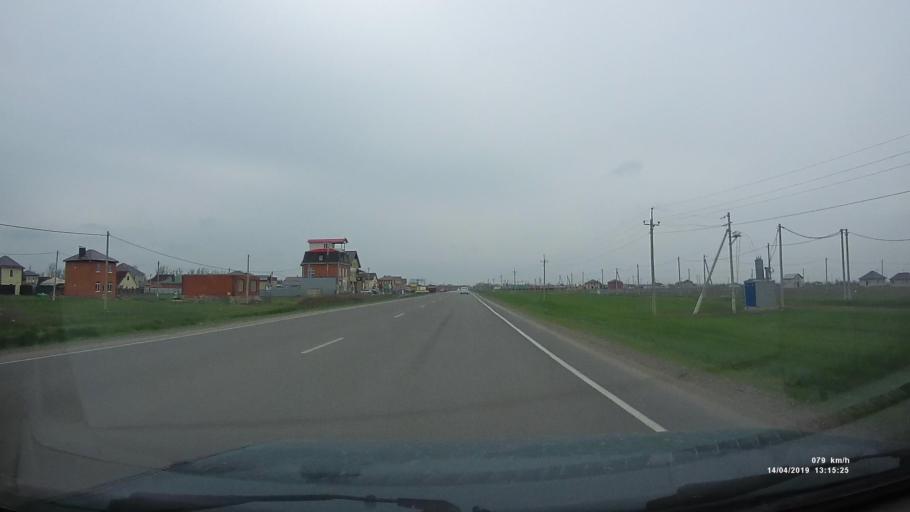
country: RU
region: Rostov
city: Kuleshovka
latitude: 47.0843
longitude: 39.5948
